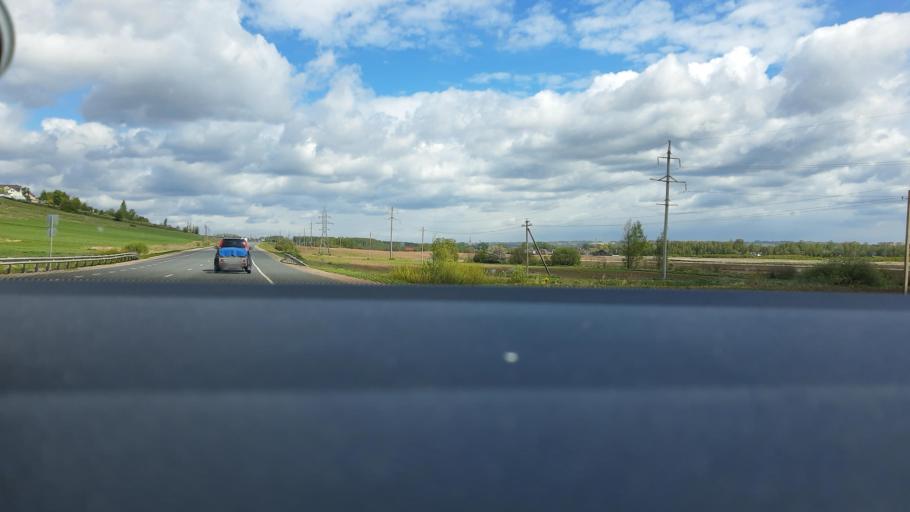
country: RU
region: Moskovskaya
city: Dmitrov
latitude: 56.3392
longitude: 37.4829
